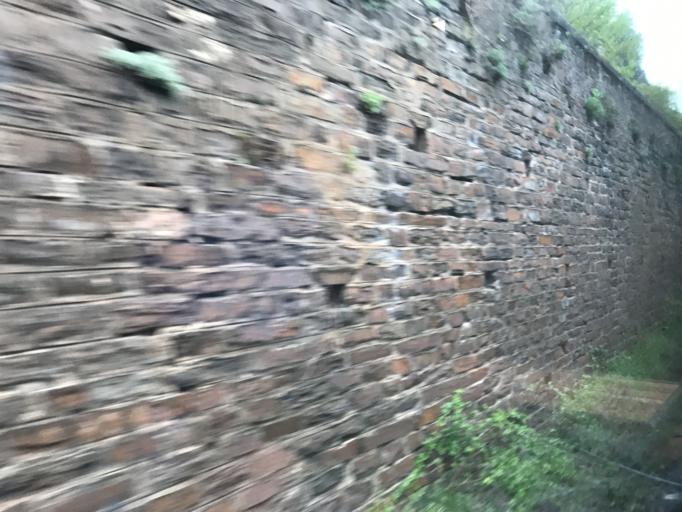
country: DE
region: Rheinland-Pfalz
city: Lof
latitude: 50.2272
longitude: 7.4320
